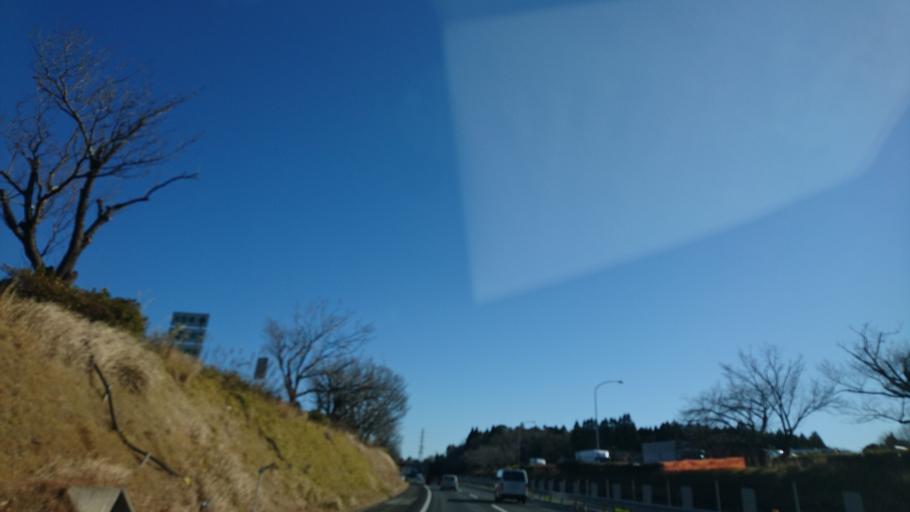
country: JP
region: Chiba
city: Oami
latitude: 35.5697
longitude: 140.2336
